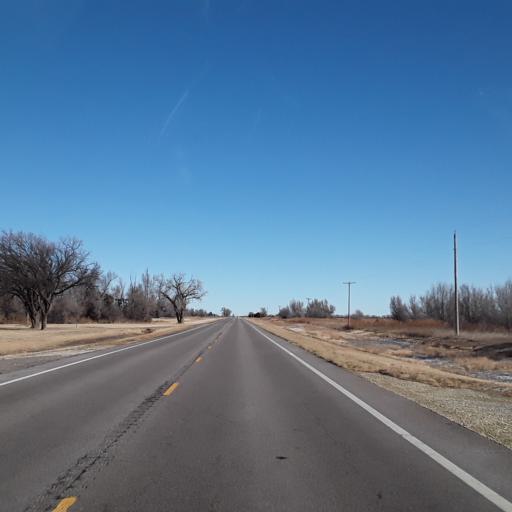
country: US
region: Kansas
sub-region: Pawnee County
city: Larned
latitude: 38.1168
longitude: -99.1839
